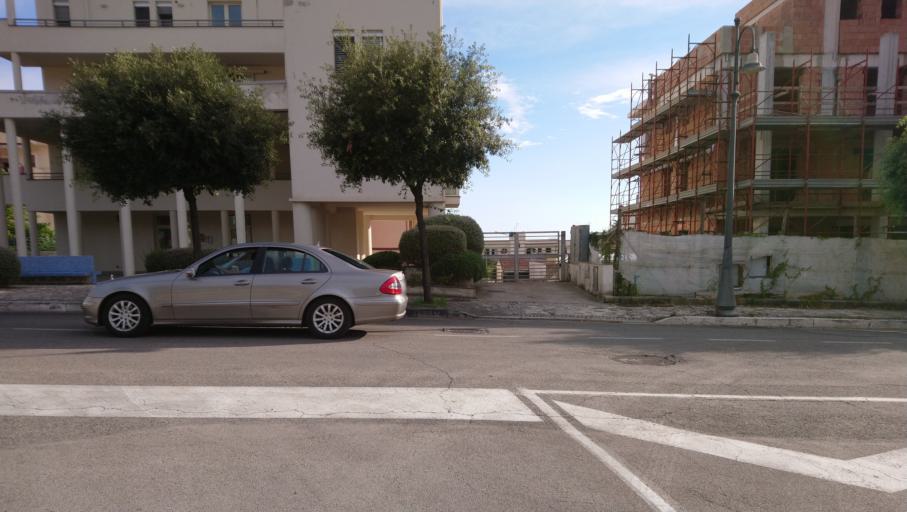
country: IT
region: Latium
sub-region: Provincia di Latina
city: Sperlonga
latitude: 41.2606
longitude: 13.4306
